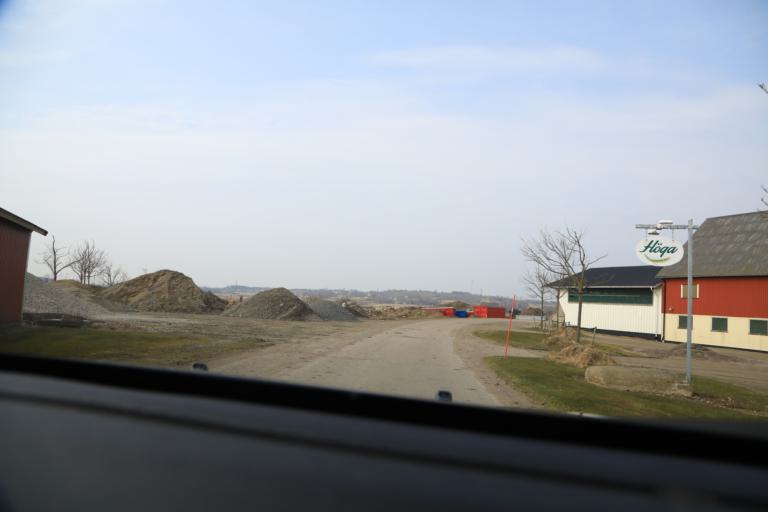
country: SE
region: Halland
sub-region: Kungsbacka Kommun
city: Frillesas
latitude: 57.2669
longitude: 12.1765
